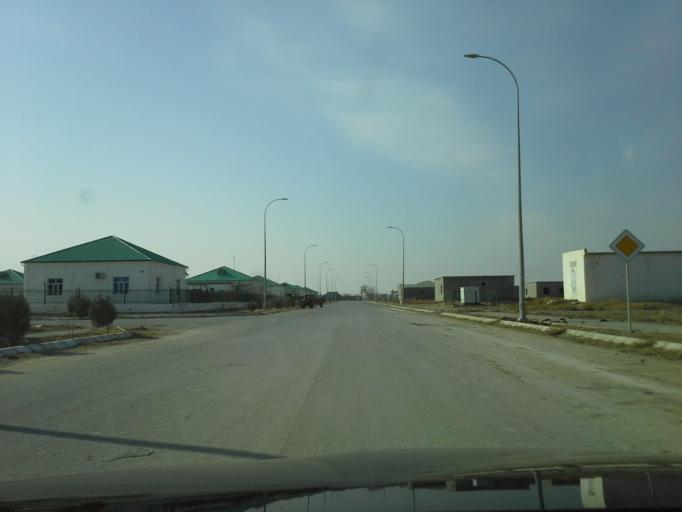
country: TM
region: Ahal
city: Abadan
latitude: 38.1743
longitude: 58.0522
